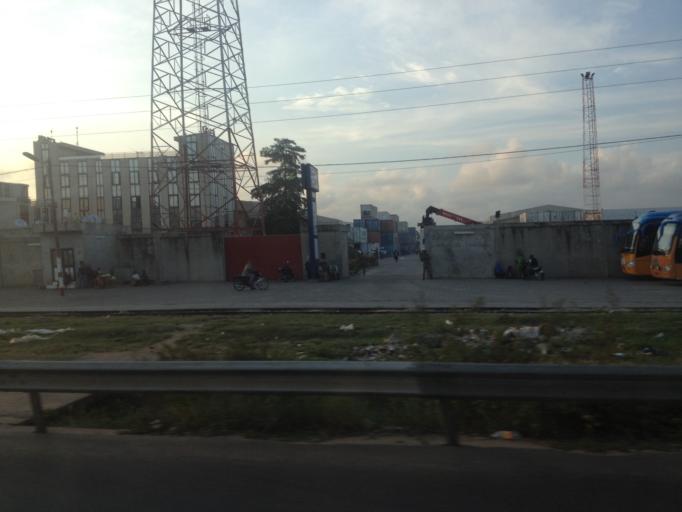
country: BJ
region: Queme
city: Porto-Novo
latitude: 6.3764
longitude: 2.5795
